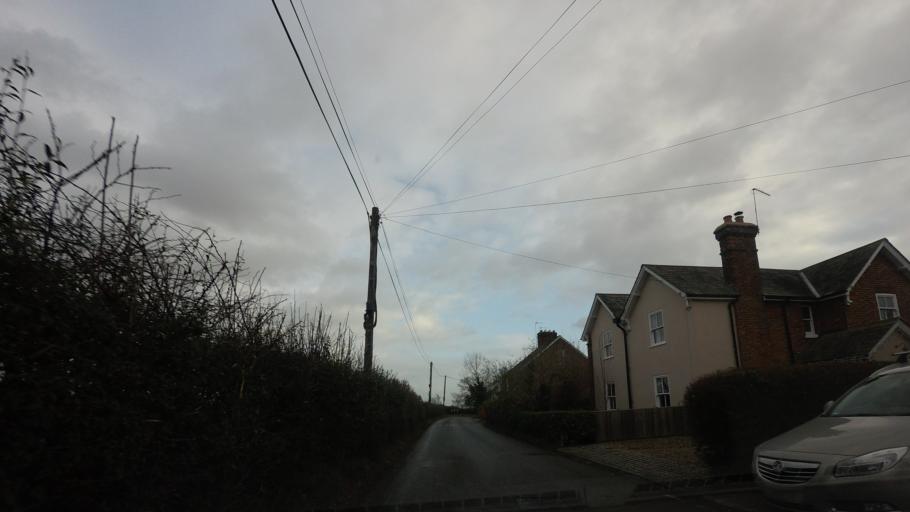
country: GB
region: England
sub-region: Kent
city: Hadlow
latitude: 51.2250
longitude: 0.3126
